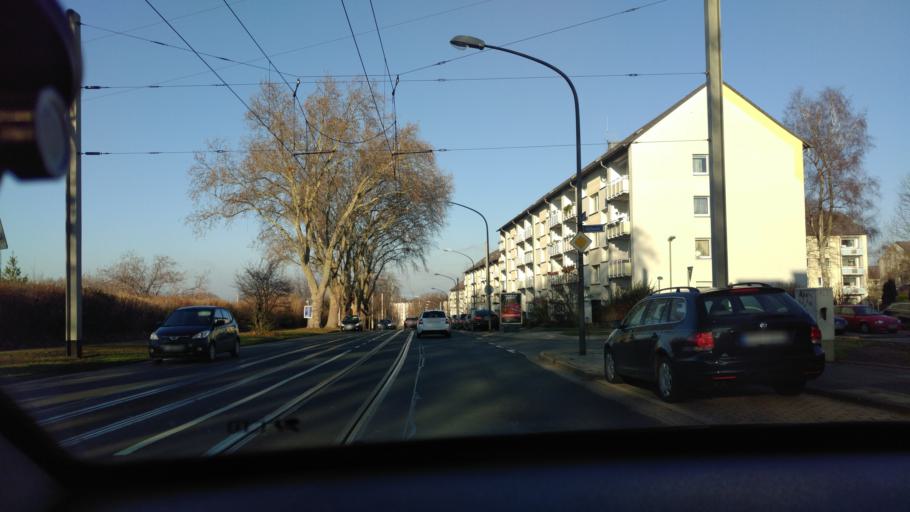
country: DE
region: North Rhine-Westphalia
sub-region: Regierungsbezirk Dusseldorf
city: Essen
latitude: 51.4766
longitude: 7.0130
